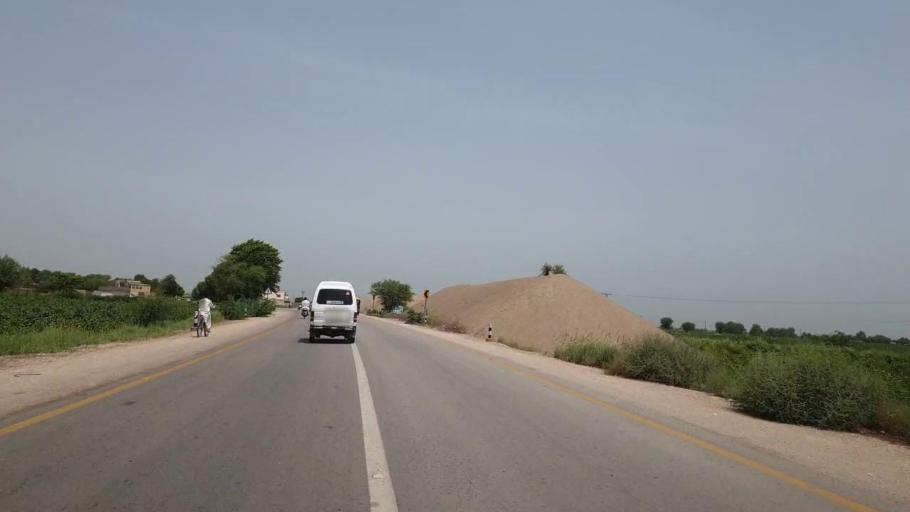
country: PK
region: Sindh
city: Shahpur Chakar
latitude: 26.1628
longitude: 68.6298
